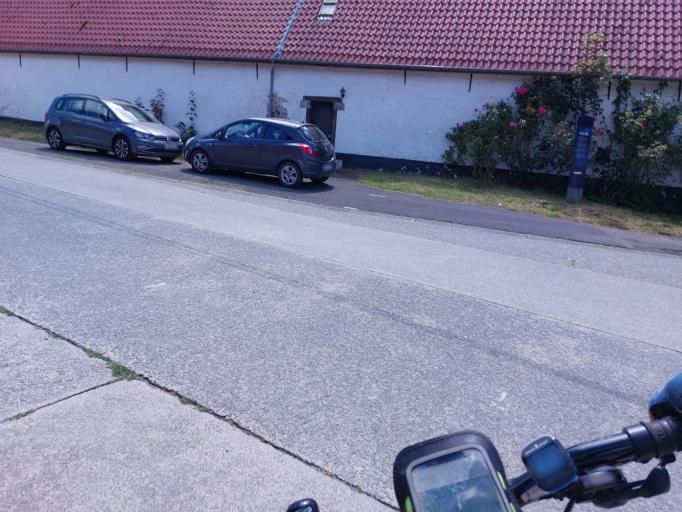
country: BE
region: Wallonia
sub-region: Province du Hainaut
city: Brugelette
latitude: 50.6052
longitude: 3.8866
